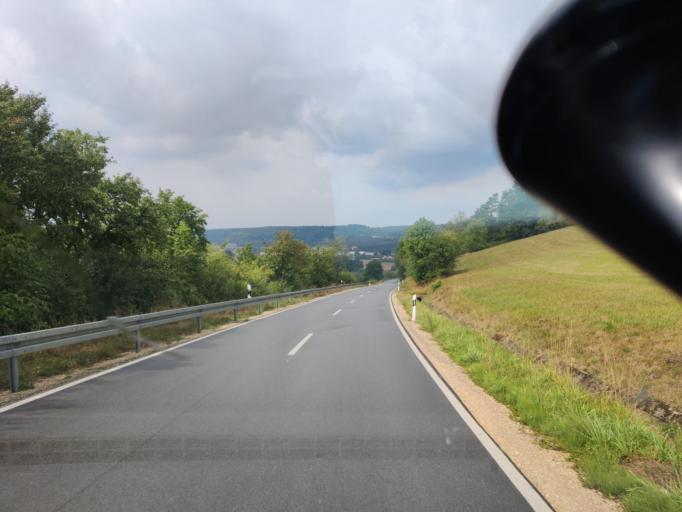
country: DE
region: Bavaria
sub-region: Regierungsbezirk Mittelfranken
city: Heideck
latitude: 49.1237
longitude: 11.1269
